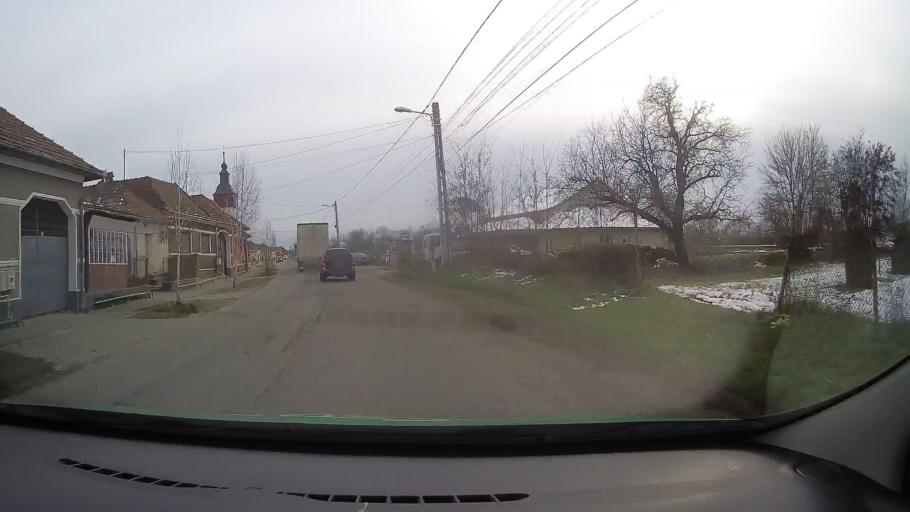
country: RO
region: Hunedoara
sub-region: Comuna Geoagiu
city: Geoagiu
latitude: 45.9019
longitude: 23.2235
